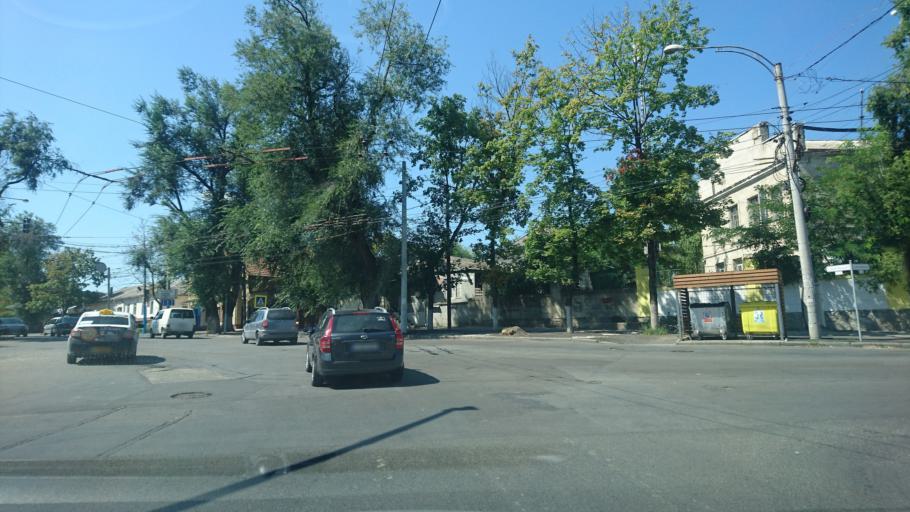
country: MD
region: Chisinau
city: Chisinau
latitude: 47.0139
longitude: 28.8282
